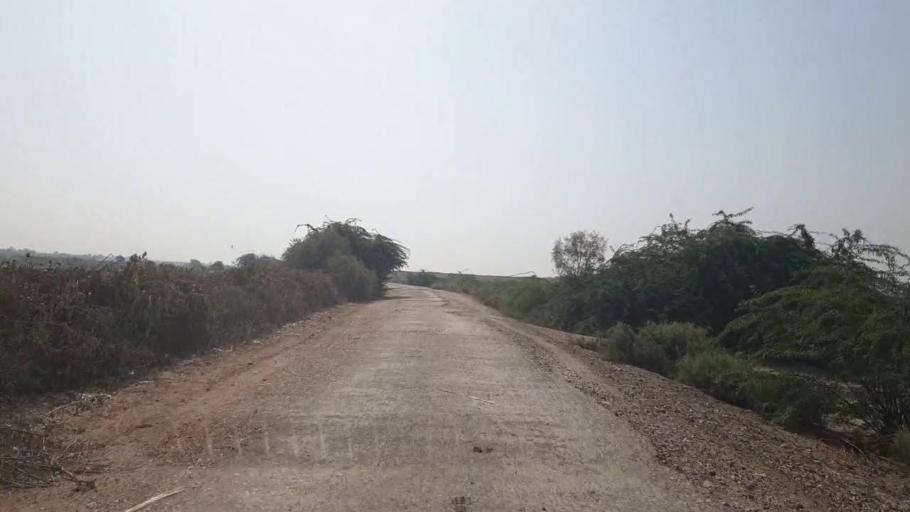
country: PK
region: Sindh
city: Berani
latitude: 25.8911
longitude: 68.7516
